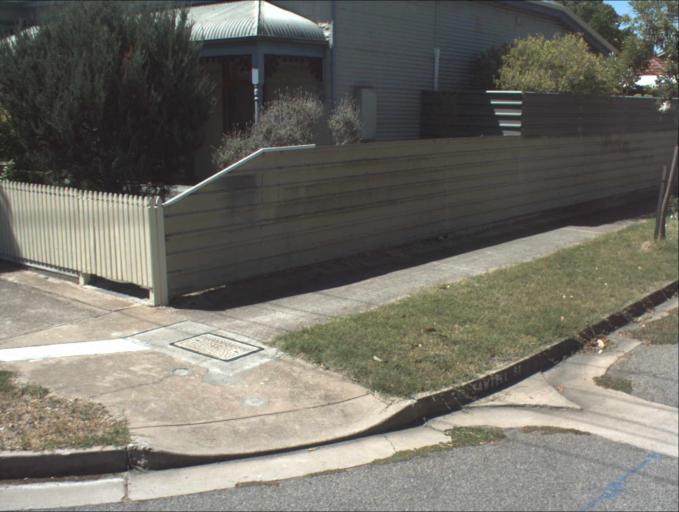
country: AU
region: South Australia
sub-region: Port Adelaide Enfield
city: Birkenhead
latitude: -34.8314
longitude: 138.4902
